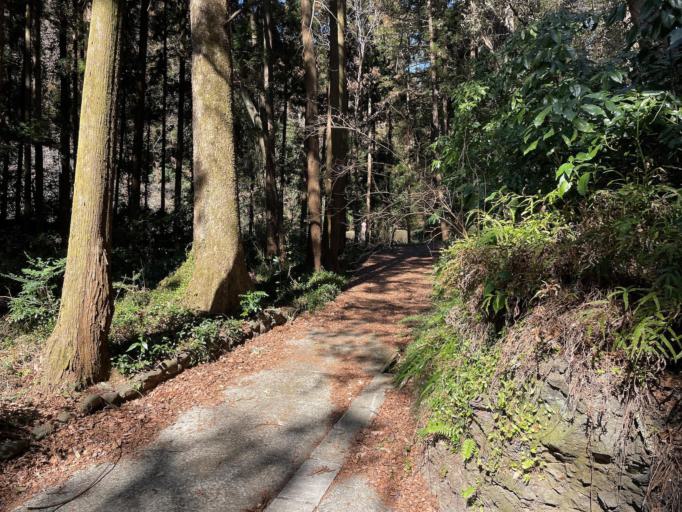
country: JP
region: Tokyo
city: Ome
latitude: 35.7915
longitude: 139.2532
